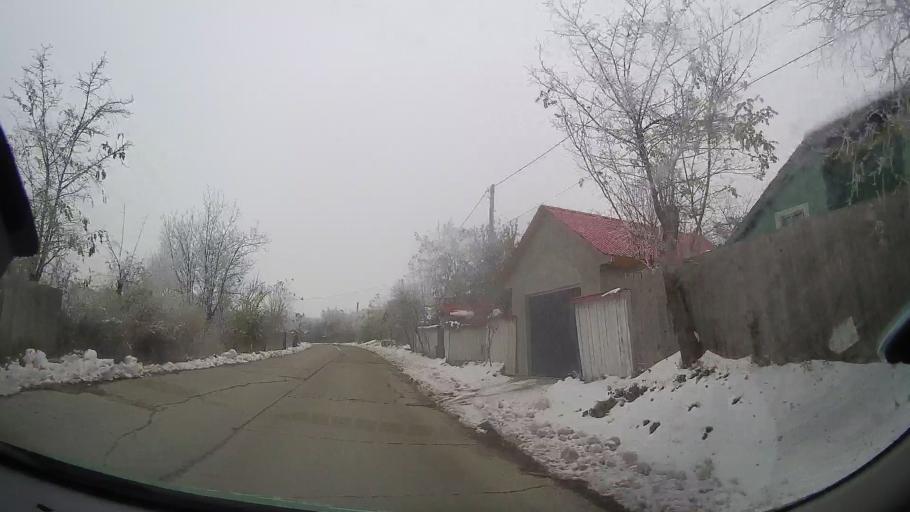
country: RO
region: Vaslui
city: Coroiesti
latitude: 46.2148
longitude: 27.4400
